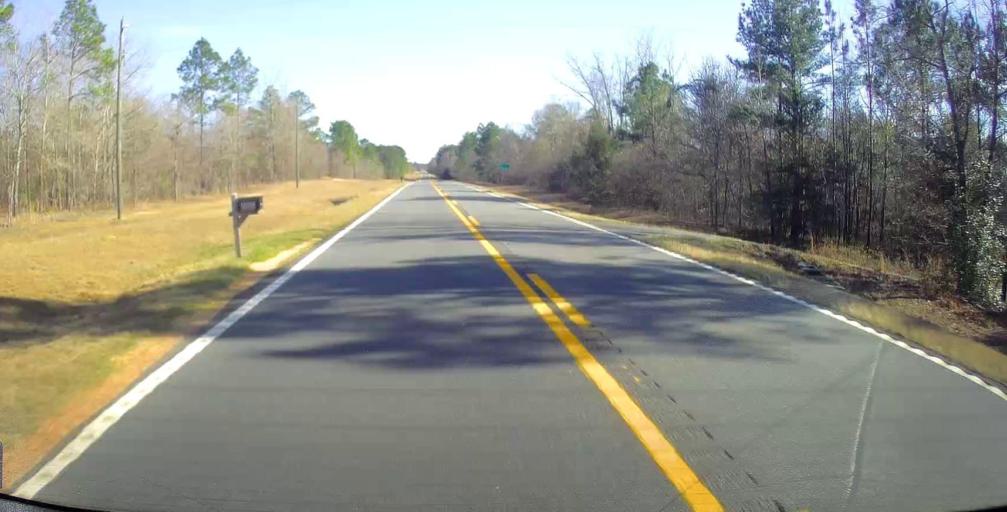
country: US
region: Georgia
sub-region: Taylor County
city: Butler
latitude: 32.4362
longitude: -84.2534
